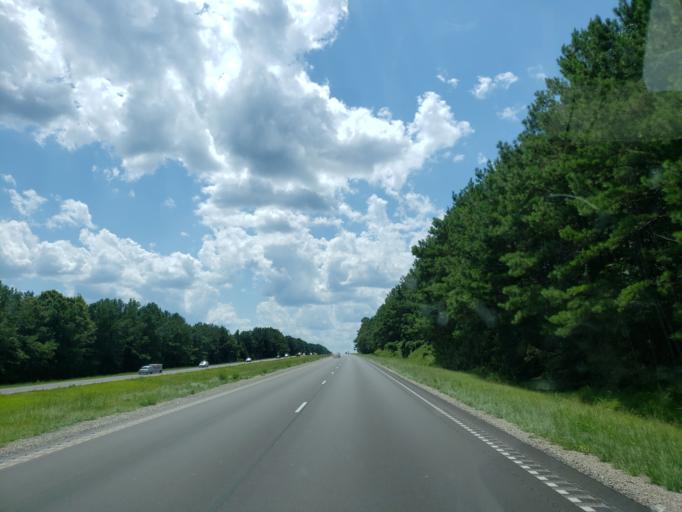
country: US
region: Mississippi
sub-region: Perry County
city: New Augusta
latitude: 31.2111
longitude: -89.1416
